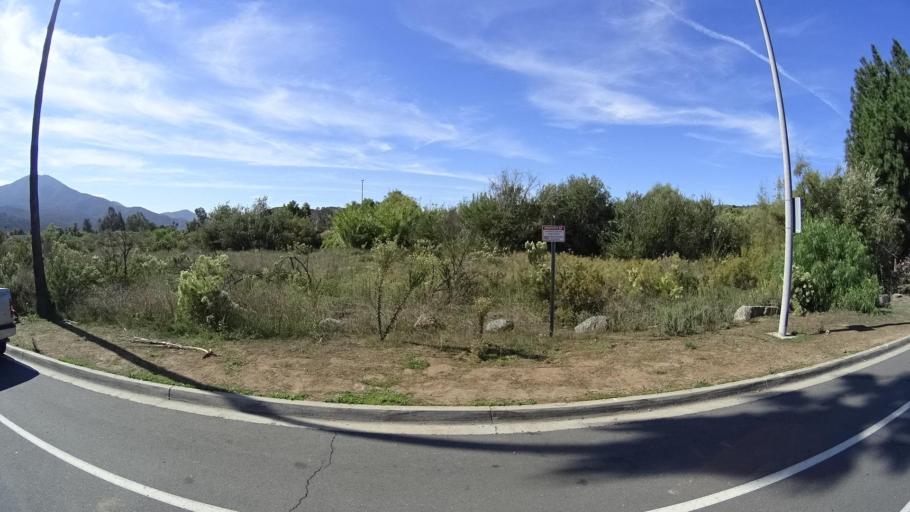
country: US
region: California
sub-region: San Diego County
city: Rancho San Diego
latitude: 32.7467
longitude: -116.9367
